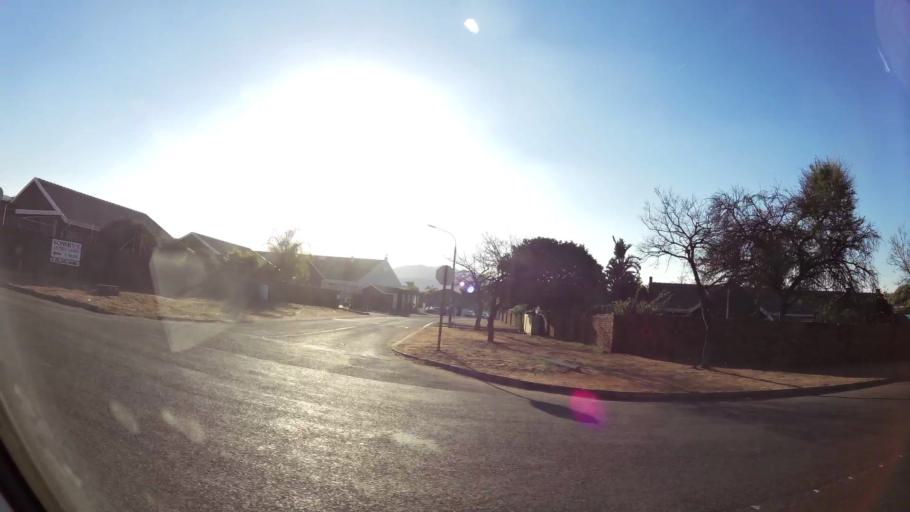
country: ZA
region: North-West
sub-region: Bojanala Platinum District Municipality
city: Rustenburg
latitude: -25.6842
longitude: 27.2164
